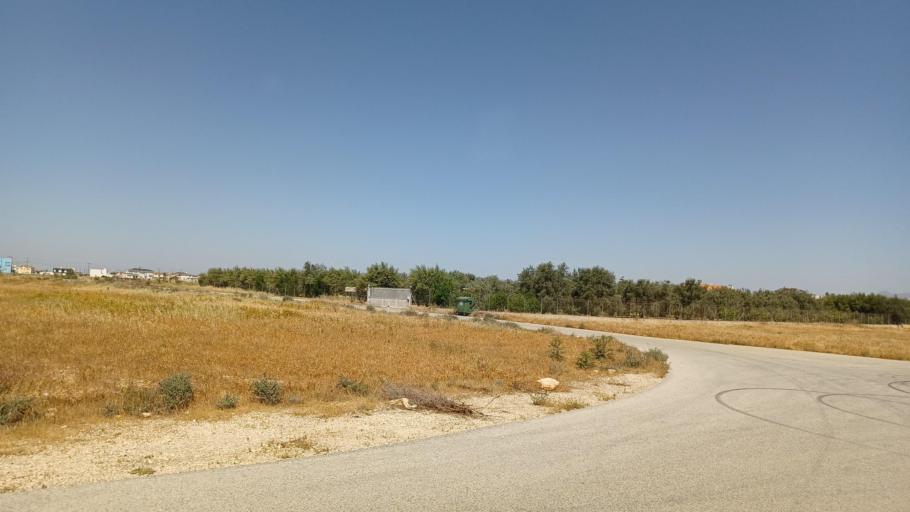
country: CY
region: Lefkosia
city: Kokkinotrimithia
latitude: 35.1560
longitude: 33.2225
